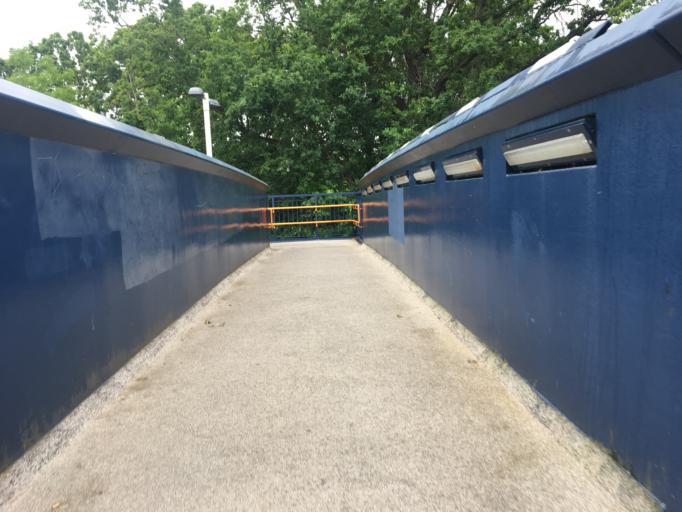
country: GB
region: England
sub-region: Surrey
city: Hinchley Wood
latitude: 51.3801
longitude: -0.3524
